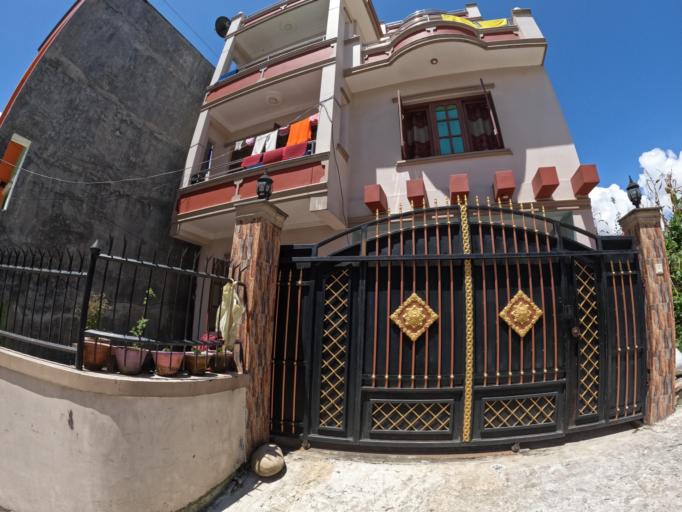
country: NP
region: Central Region
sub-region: Bagmati Zone
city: Kathmandu
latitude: 27.7515
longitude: 85.3291
